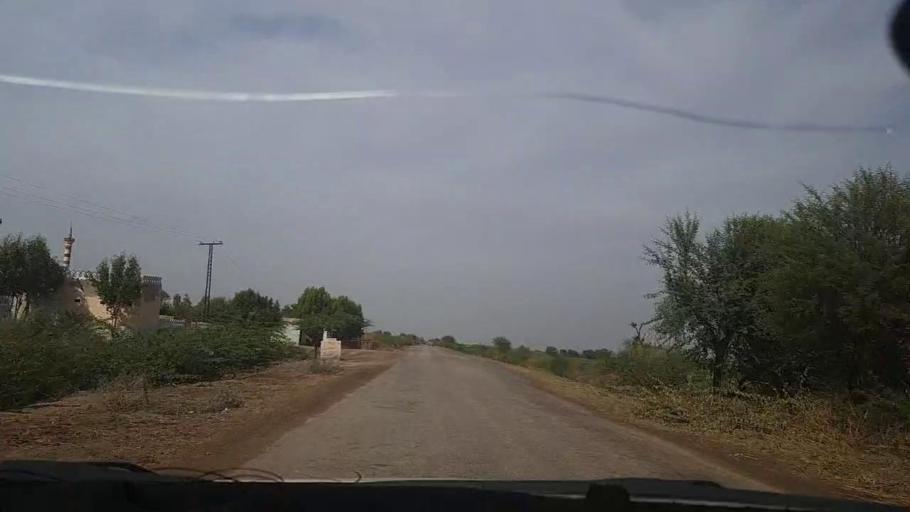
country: PK
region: Sindh
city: Pithoro
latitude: 25.5645
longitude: 69.3629
